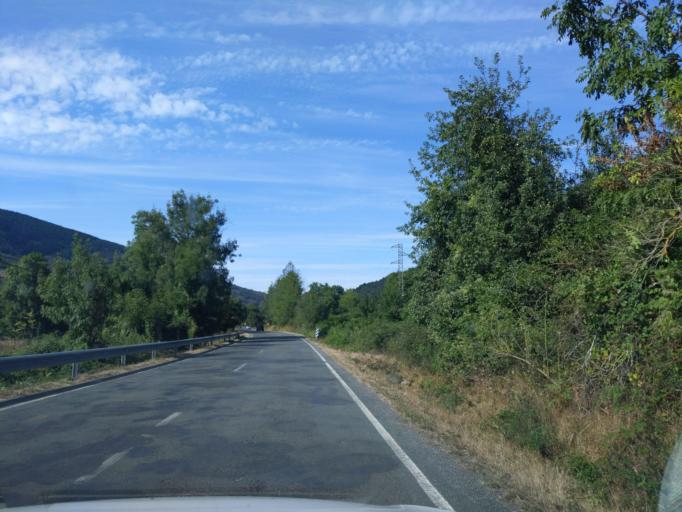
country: ES
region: La Rioja
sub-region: Provincia de La Rioja
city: Ezcaray
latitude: 42.2854
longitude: -3.0265
